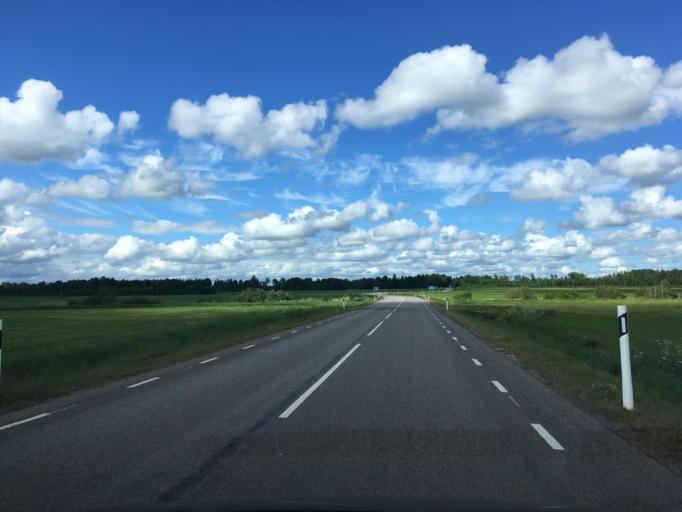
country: EE
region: Paernumaa
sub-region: Halinga vald
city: Parnu-Jaagupi
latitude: 58.6568
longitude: 24.5751
